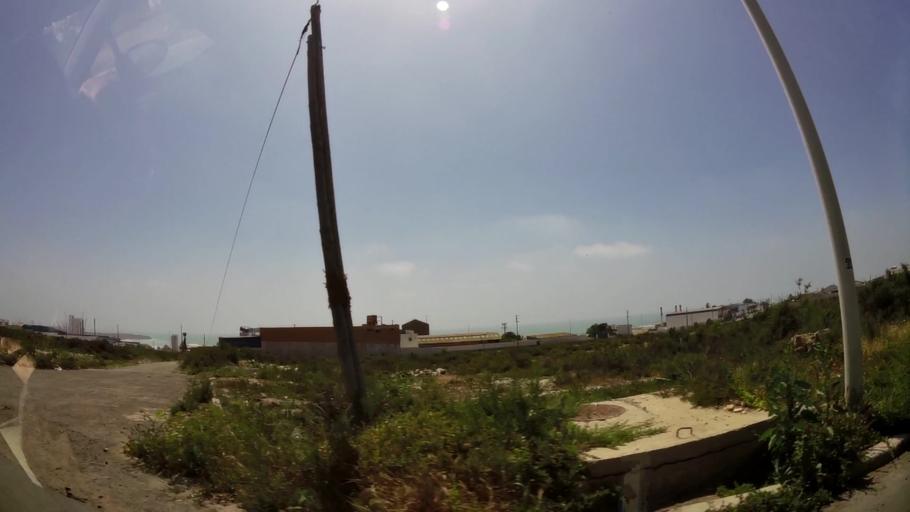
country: MA
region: Souss-Massa-Draa
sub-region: Agadir-Ida-ou-Tnan
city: Aourir
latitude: 30.4412
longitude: -9.6469
